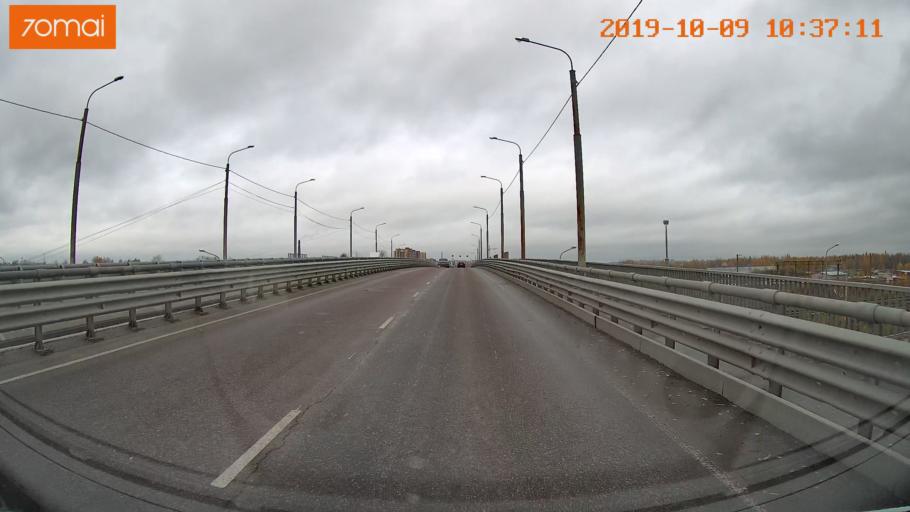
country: RU
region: Vologda
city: Vologda
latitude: 59.2341
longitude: 39.8656
